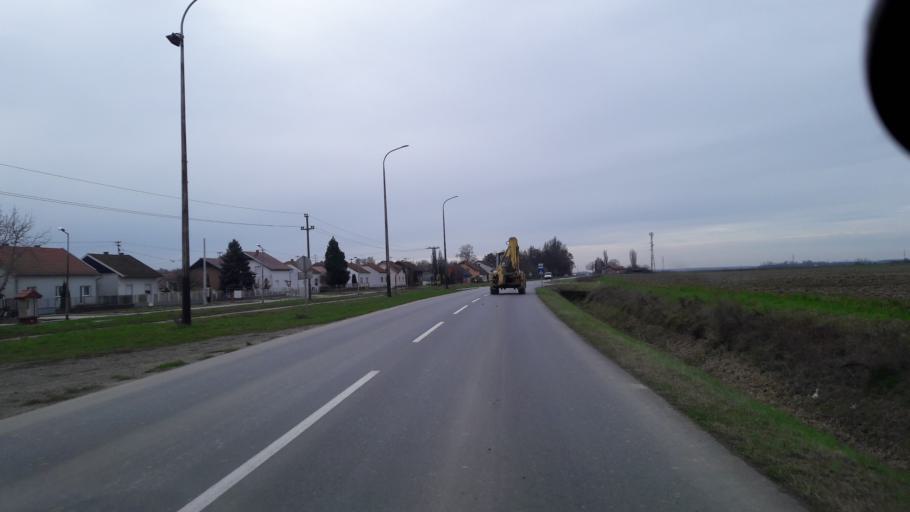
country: HR
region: Osjecko-Baranjska
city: Ovcara
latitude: 45.5090
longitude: 18.5667
